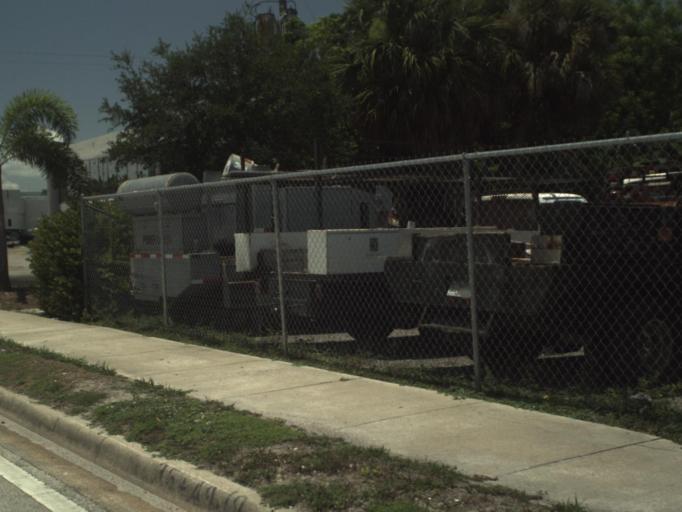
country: US
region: Florida
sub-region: Martin County
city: Stuart
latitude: 27.1797
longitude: -80.2367
